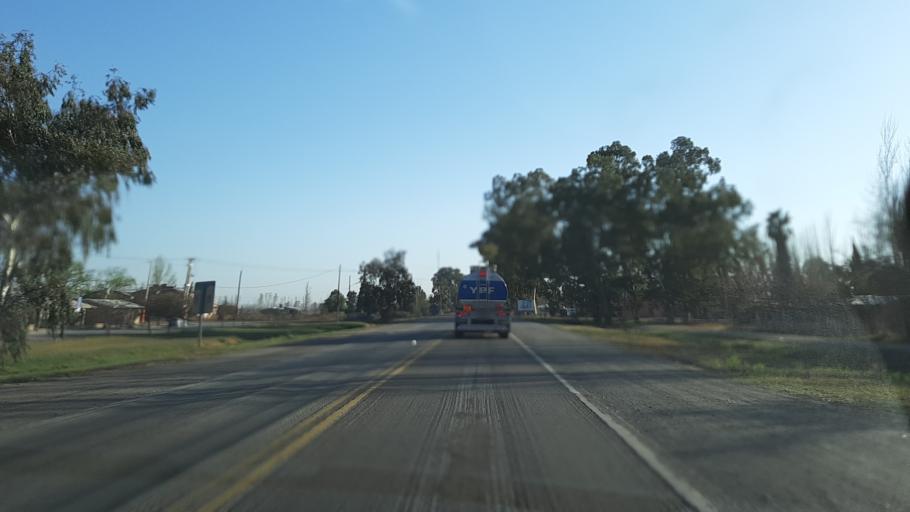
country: AR
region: Mendoza
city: General Lavalle
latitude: -32.5858
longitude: -68.6677
